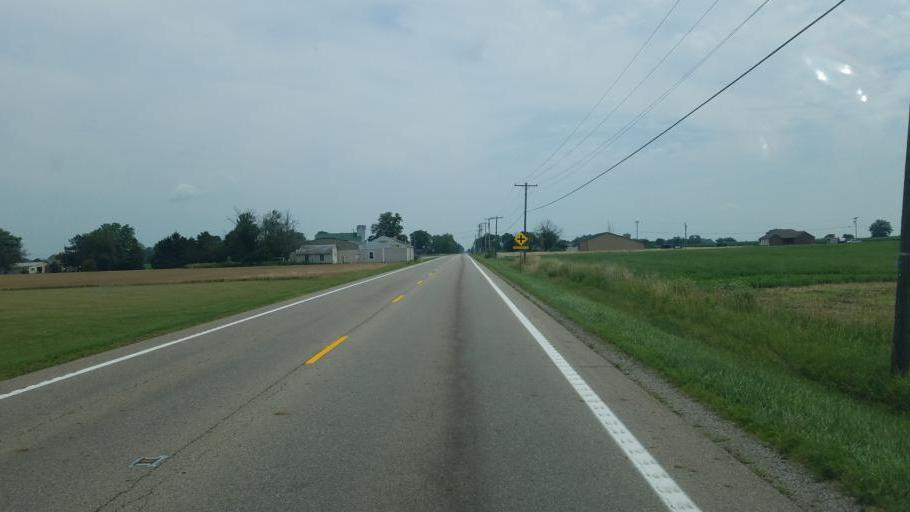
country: US
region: Ohio
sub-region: Madison County
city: West Jefferson
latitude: 39.9867
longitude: -83.3392
